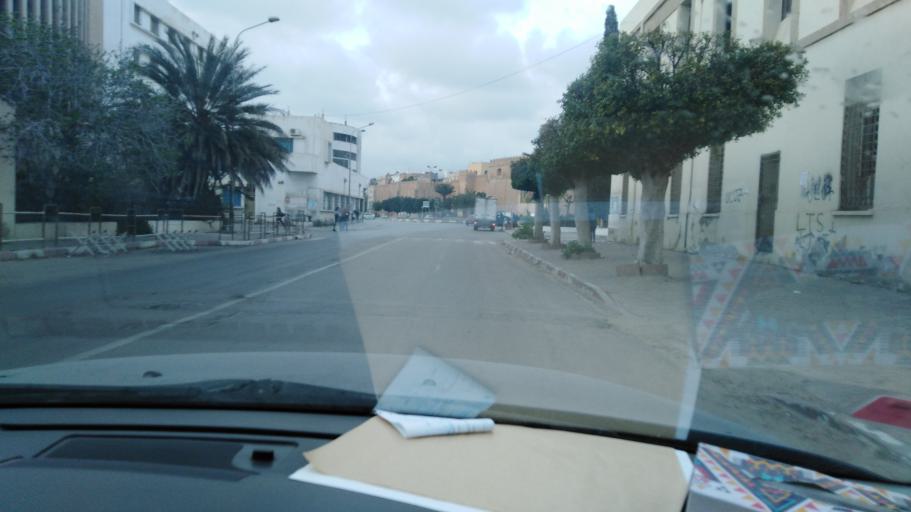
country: TN
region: Safaqis
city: Sfax
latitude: 34.7321
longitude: 10.7584
